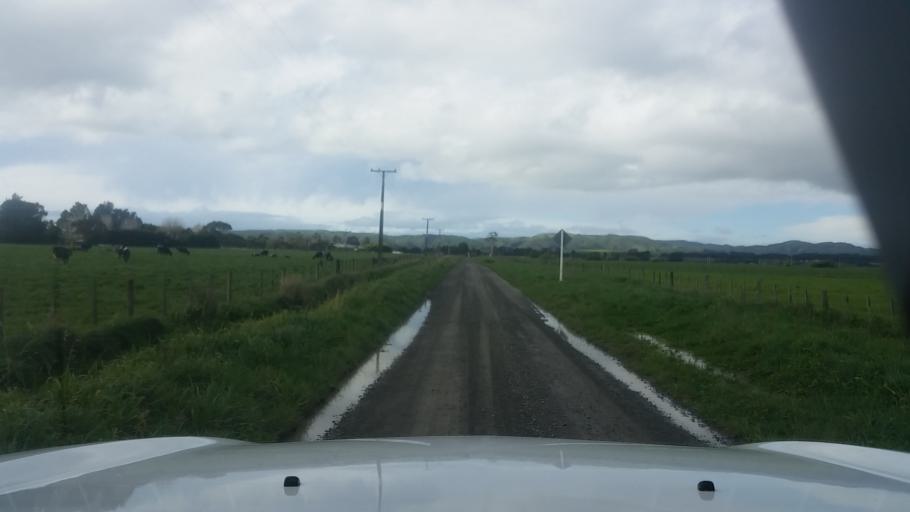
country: NZ
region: Wellington
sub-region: South Wairarapa District
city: Waipawa
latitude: -41.1431
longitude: 175.4150
